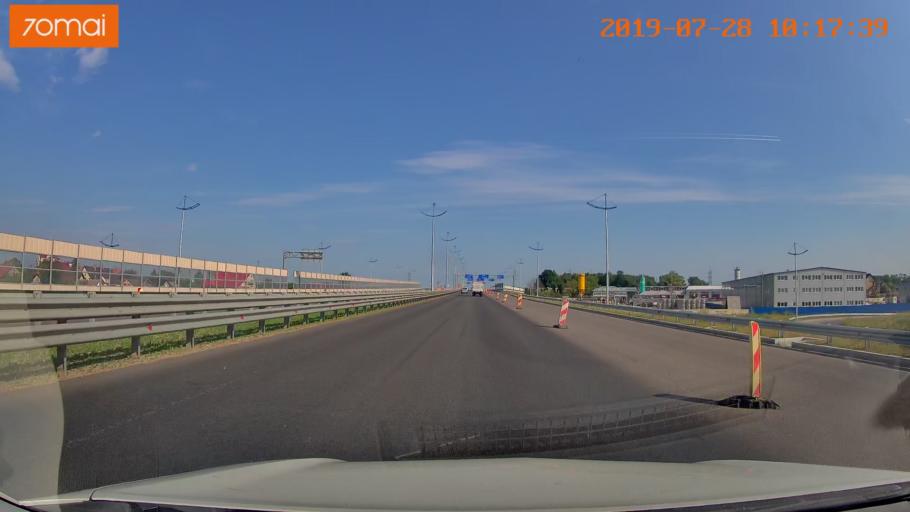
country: RU
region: Kaliningrad
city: Maloye Isakovo
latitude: 54.7426
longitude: 20.5932
